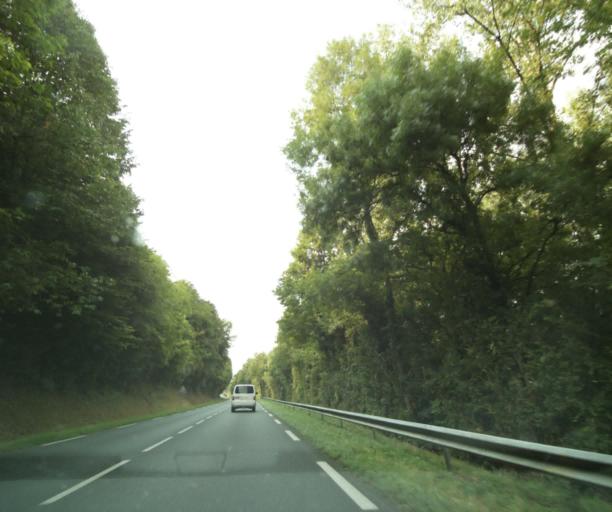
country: FR
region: Centre
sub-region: Departement de l'Indre
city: Clion
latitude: 46.9642
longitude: 1.2053
